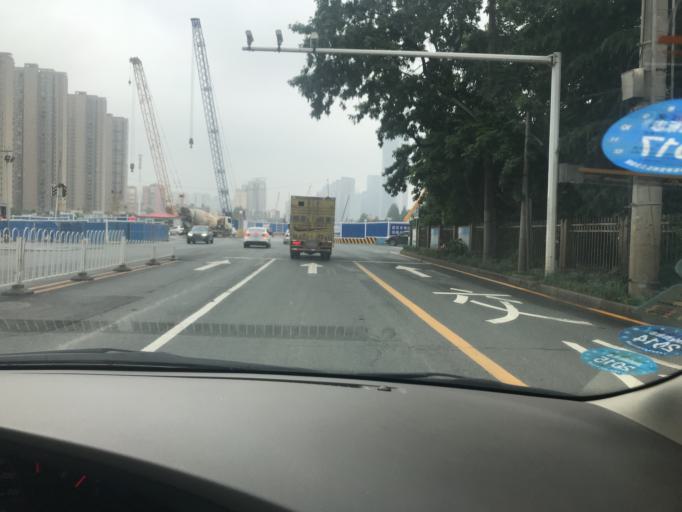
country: CN
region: Hubei
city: Jiang'an
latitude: 30.5953
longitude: 114.3306
